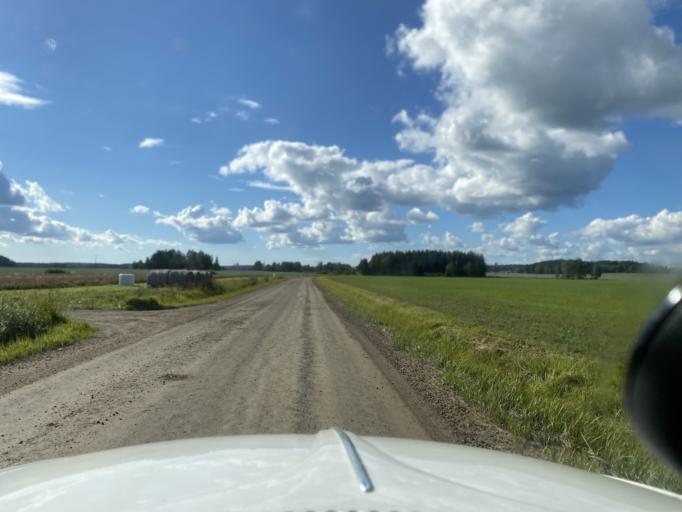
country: FI
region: Pirkanmaa
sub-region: Lounais-Pirkanmaa
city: Punkalaidun
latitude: 61.1295
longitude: 23.2439
